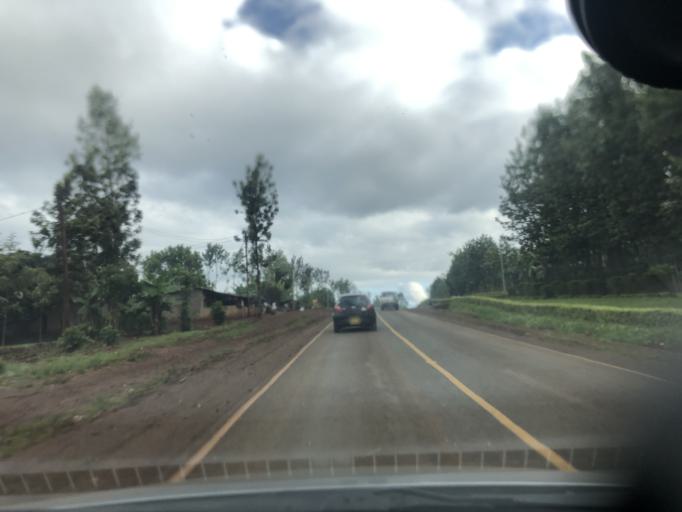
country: KE
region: Murang'a District
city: Maragua
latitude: -0.8285
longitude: 37.1377
